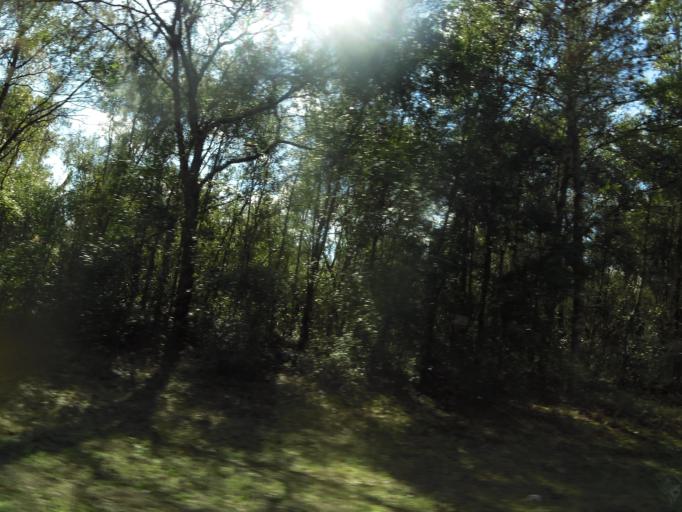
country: US
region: Florida
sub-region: Volusia County
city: De Leon Springs
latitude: 29.1384
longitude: -81.3566
